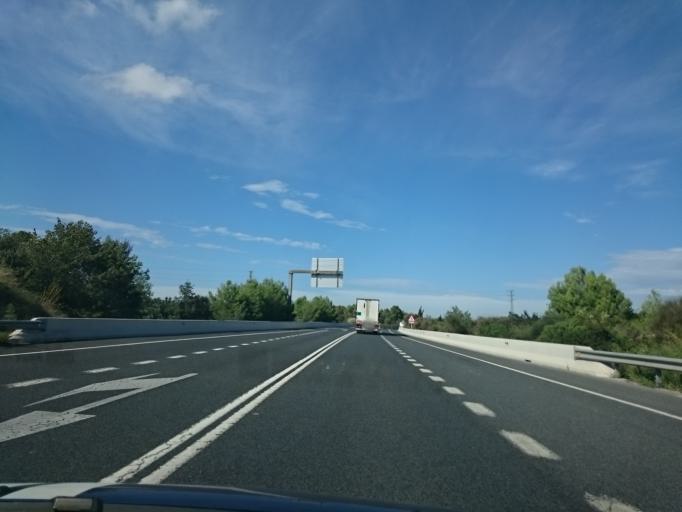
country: ES
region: Catalonia
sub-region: Provincia de Barcelona
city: Castellet
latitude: 41.3147
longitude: 1.6406
